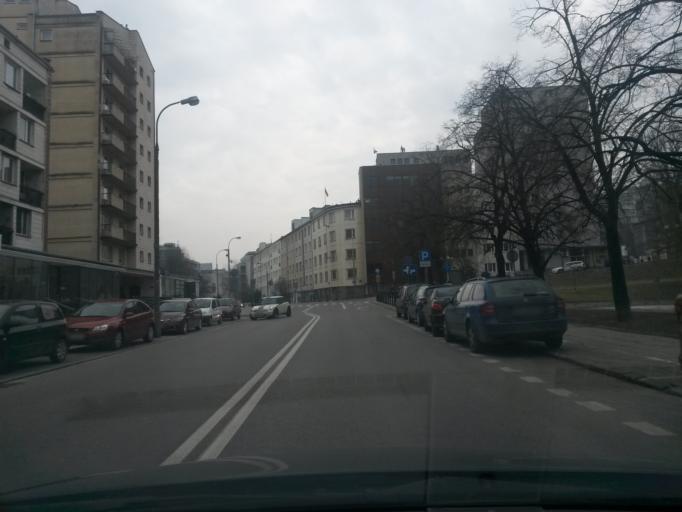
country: PL
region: Masovian Voivodeship
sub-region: Warszawa
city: Srodmiescie
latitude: 52.2405
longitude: 21.0226
